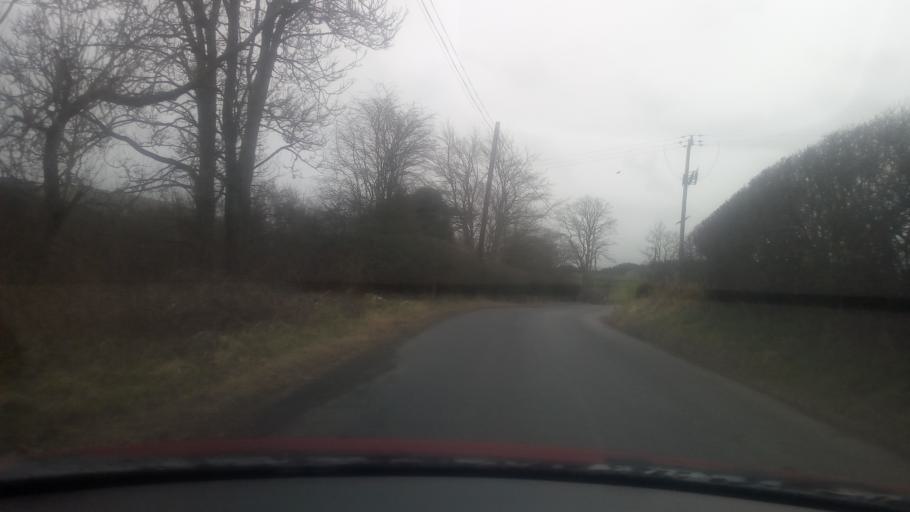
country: GB
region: Scotland
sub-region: The Scottish Borders
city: Hawick
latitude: 55.3956
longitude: -2.6565
